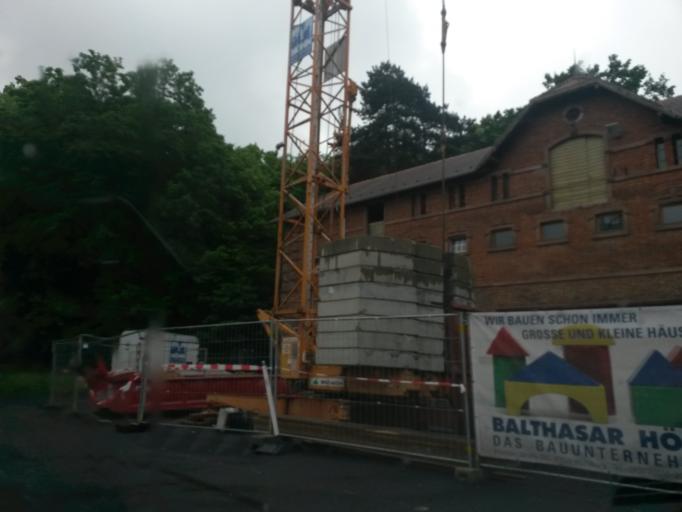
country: DE
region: Bavaria
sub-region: Regierungsbezirk Unterfranken
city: Hochberg
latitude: 49.7938
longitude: 9.8938
